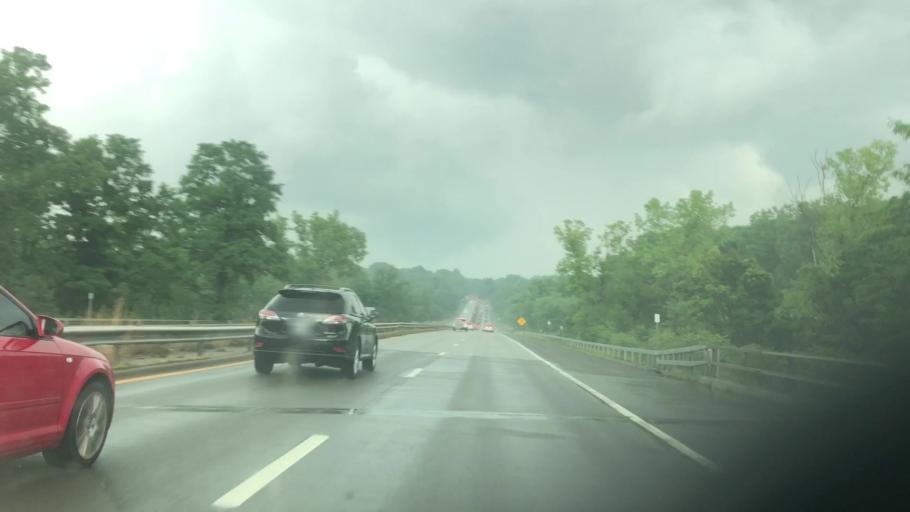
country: US
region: New York
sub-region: Monroe County
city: East Rochester
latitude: 43.1276
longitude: -77.4942
